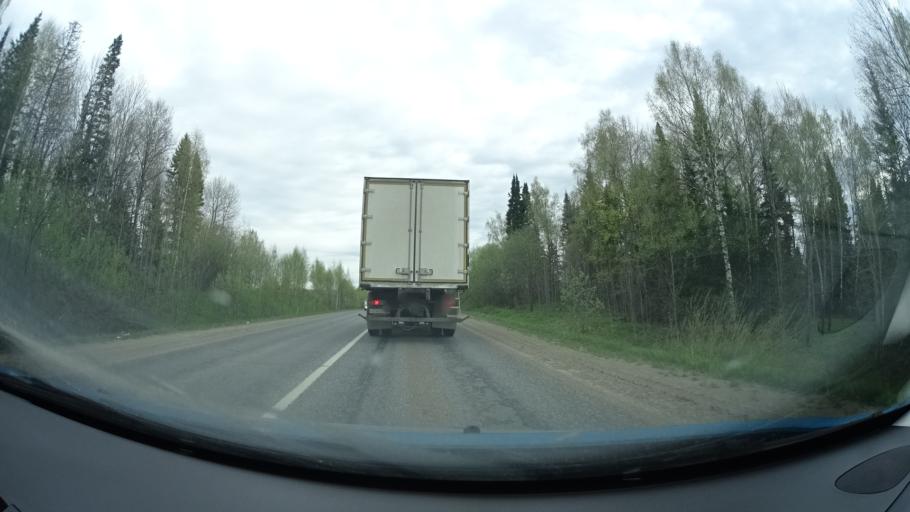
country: RU
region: Perm
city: Yugo-Kamskiy
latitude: 57.5811
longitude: 55.6777
